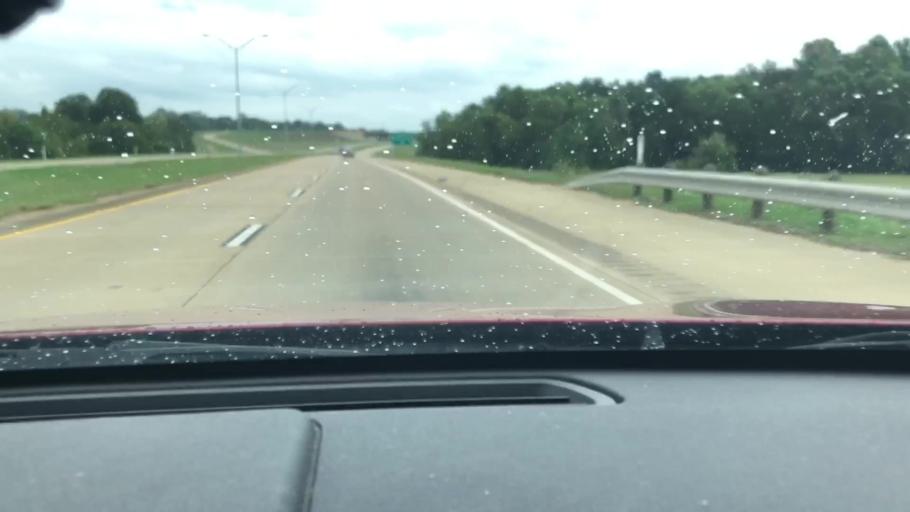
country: US
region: Texas
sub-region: Bowie County
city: Texarkana
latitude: 33.3850
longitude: -94.0506
